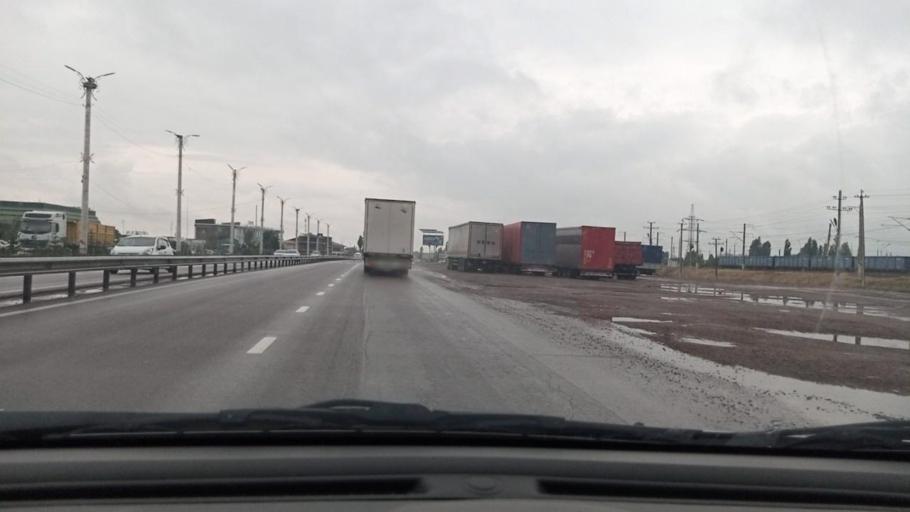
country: UZ
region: Toshkent
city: Ohangaron
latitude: 40.8992
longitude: 69.6660
